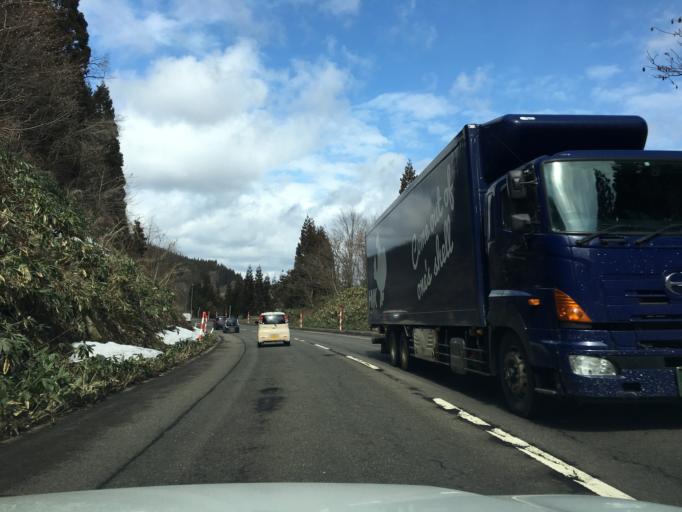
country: JP
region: Akita
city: Takanosu
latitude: 40.0133
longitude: 140.2787
